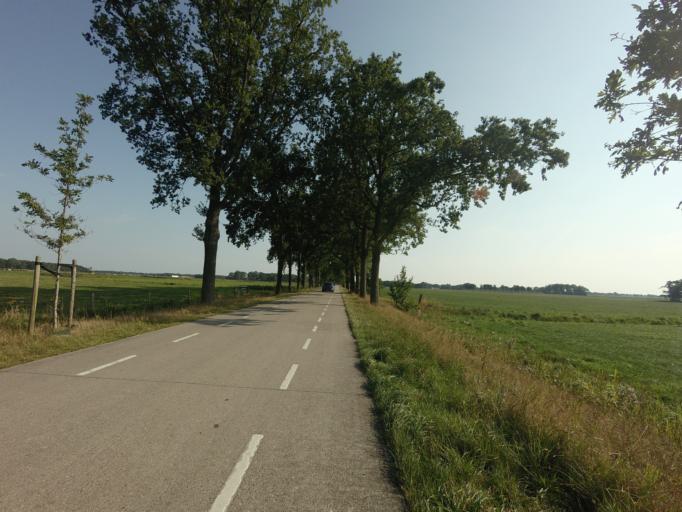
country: NL
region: Groningen
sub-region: Gemeente Zuidhorn
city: Aduard
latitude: 53.1803
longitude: 6.4733
